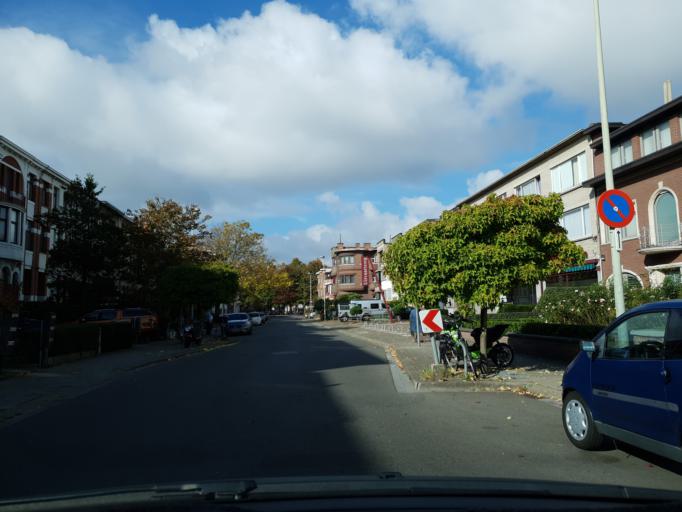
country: BE
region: Flanders
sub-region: Provincie Antwerpen
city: Schoten
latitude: 51.2505
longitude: 4.4514
